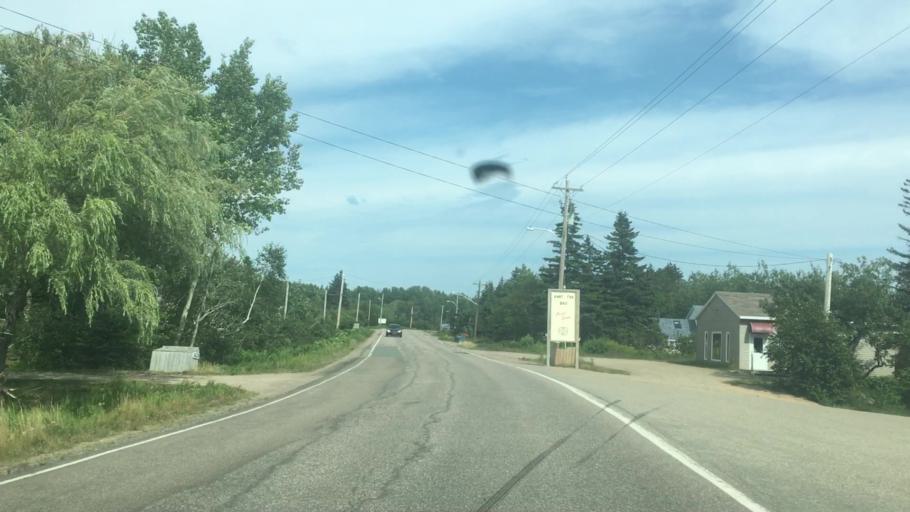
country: CA
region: Nova Scotia
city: Sydney Mines
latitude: 46.6904
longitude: -60.3817
